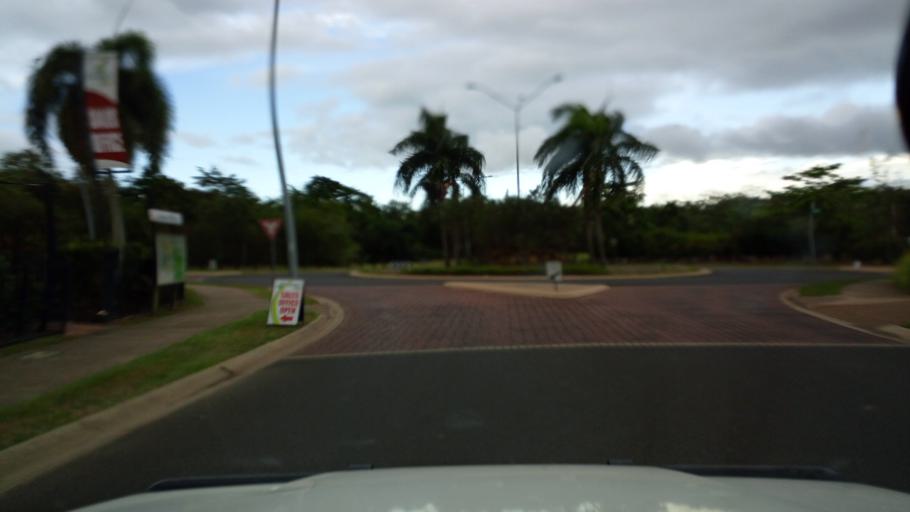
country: AU
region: Queensland
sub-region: Cairns
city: Redlynch
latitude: -16.8410
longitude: 145.6893
